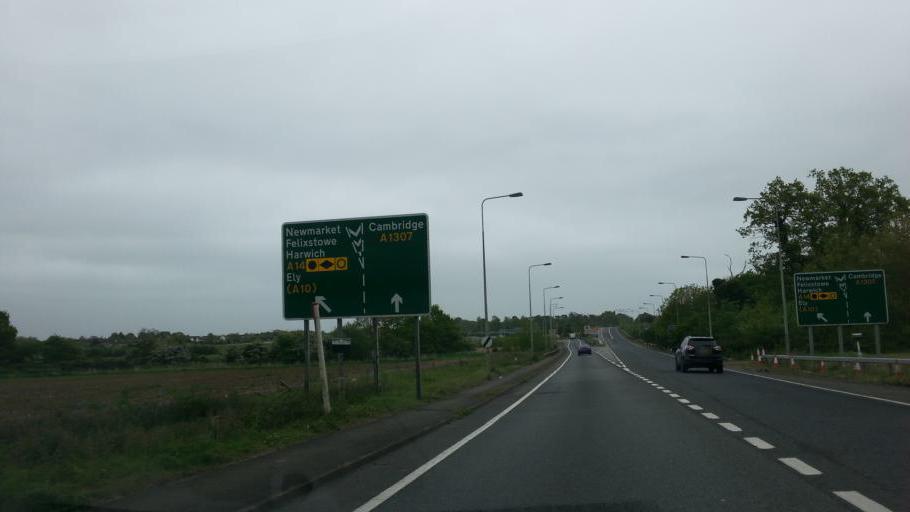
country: GB
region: England
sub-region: Cambridgeshire
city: Girton
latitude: 52.2345
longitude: 0.0698
